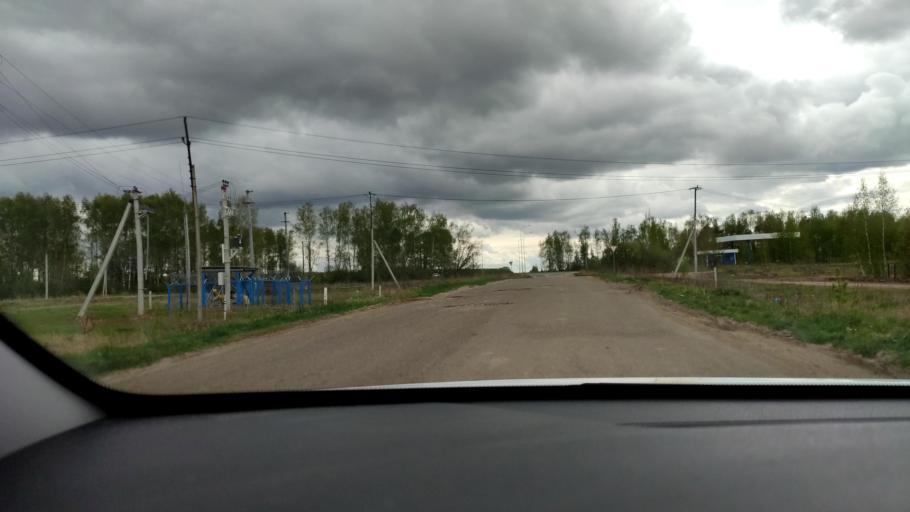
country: RU
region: Tatarstan
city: Vysokaya Gora
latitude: 55.8026
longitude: 49.3130
